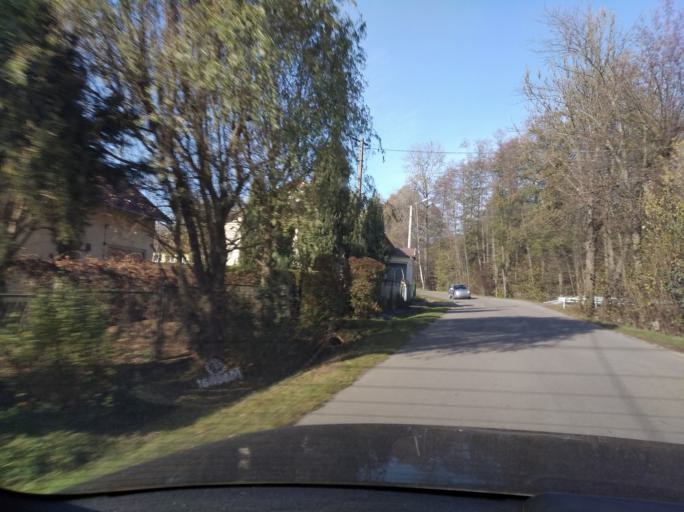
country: PL
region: Subcarpathian Voivodeship
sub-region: Powiat strzyzowski
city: Frysztak
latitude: 49.8848
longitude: 21.6067
